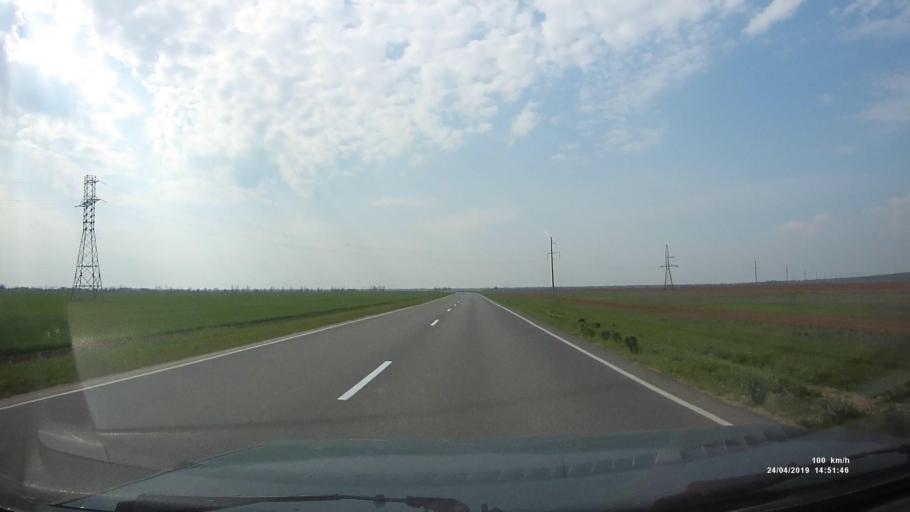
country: RU
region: Rostov
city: Remontnoye
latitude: 46.5273
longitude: 43.6945
